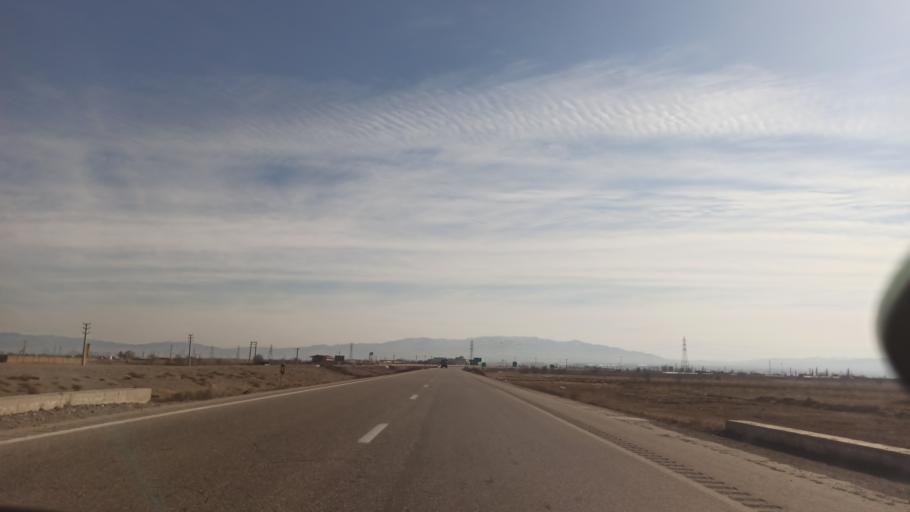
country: IR
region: Qazvin
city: Bu'in Zahra
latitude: 35.7775
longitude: 50.0833
